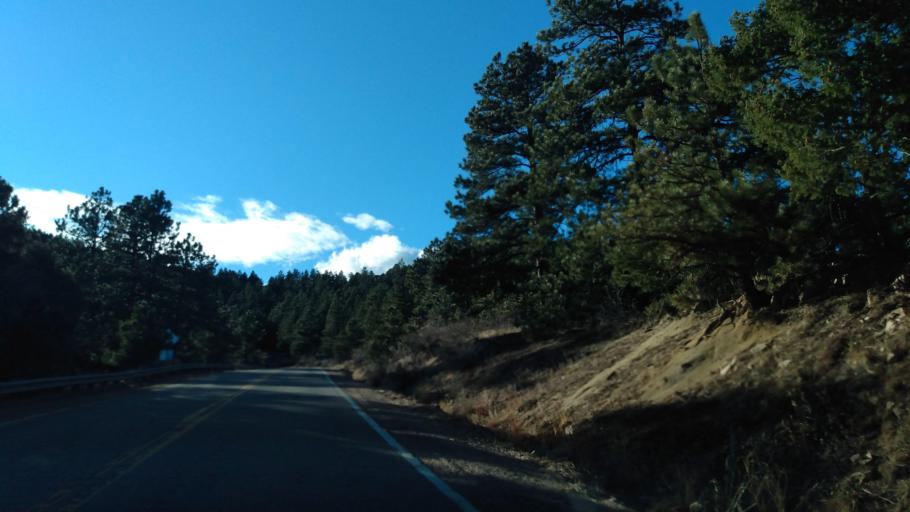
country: US
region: Colorado
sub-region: Boulder County
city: Boulder
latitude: 40.0014
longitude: -105.3569
